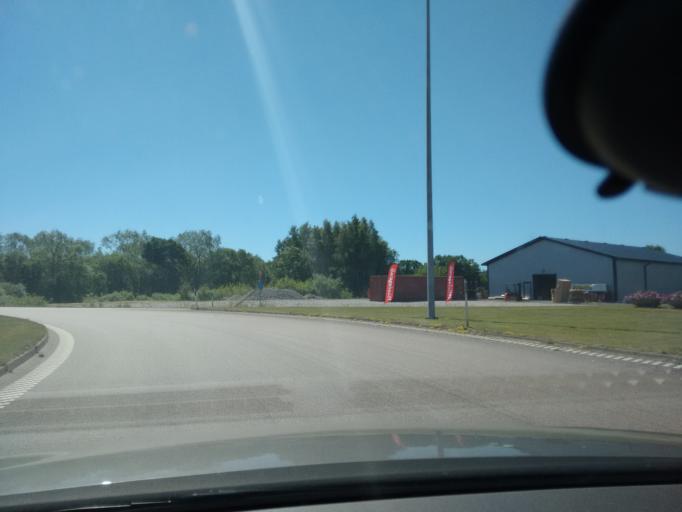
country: SE
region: Skane
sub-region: Horby Kommun
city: Hoerby
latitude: 55.8496
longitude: 13.6446
